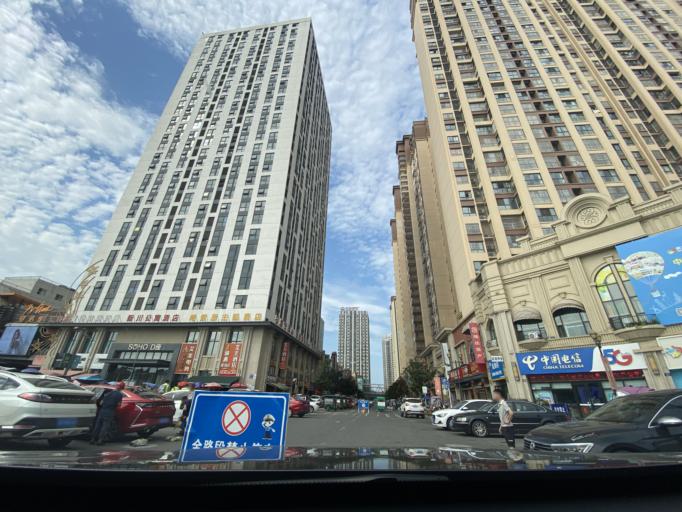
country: CN
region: Sichuan
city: Mianyang
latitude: 31.4126
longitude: 104.7819
